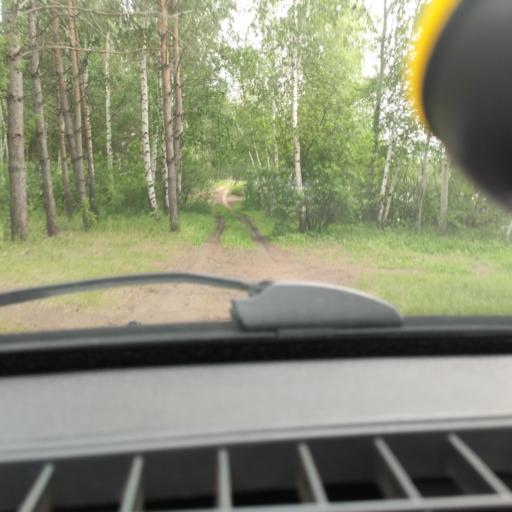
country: RU
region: Samara
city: Zhigulevsk
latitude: 53.5041
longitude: 49.5016
